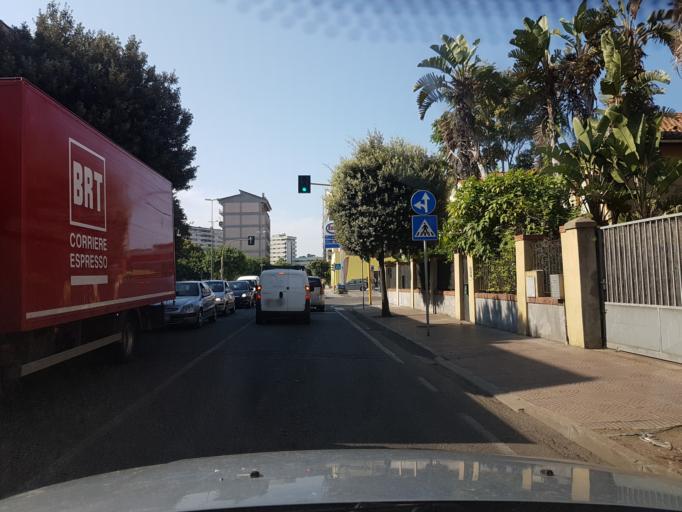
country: IT
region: Sardinia
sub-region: Provincia di Oristano
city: Oristano
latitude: 39.9050
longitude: 8.5883
